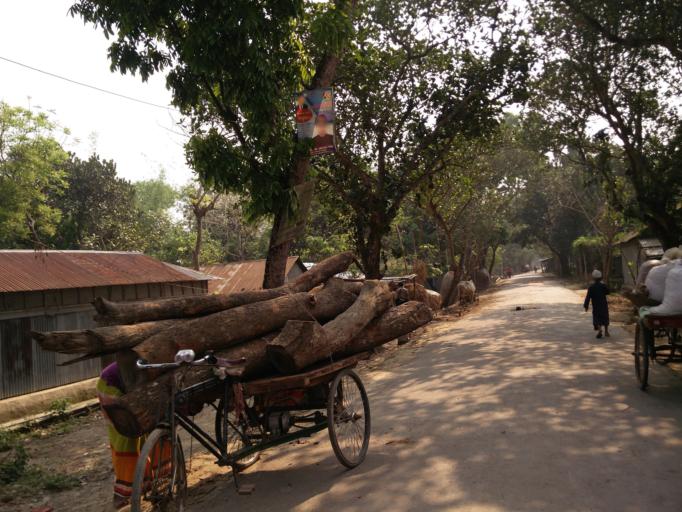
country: BD
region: Dhaka
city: Sherpur
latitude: 24.9108
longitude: 90.1559
